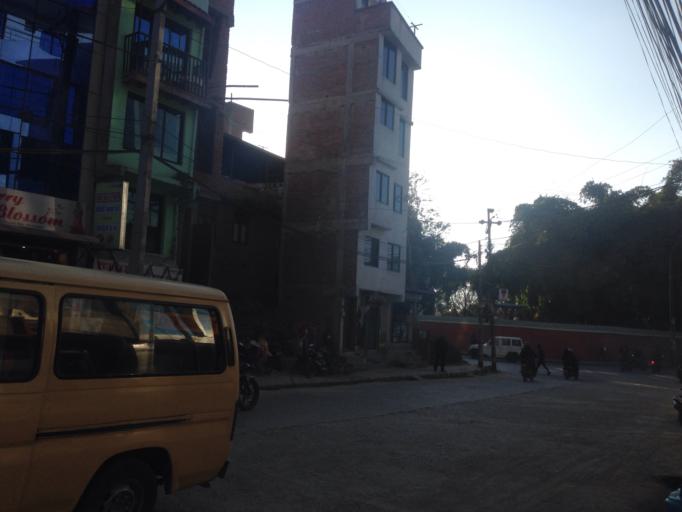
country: NP
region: Central Region
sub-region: Bagmati Zone
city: Kathmandu
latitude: 27.7173
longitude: 85.3254
